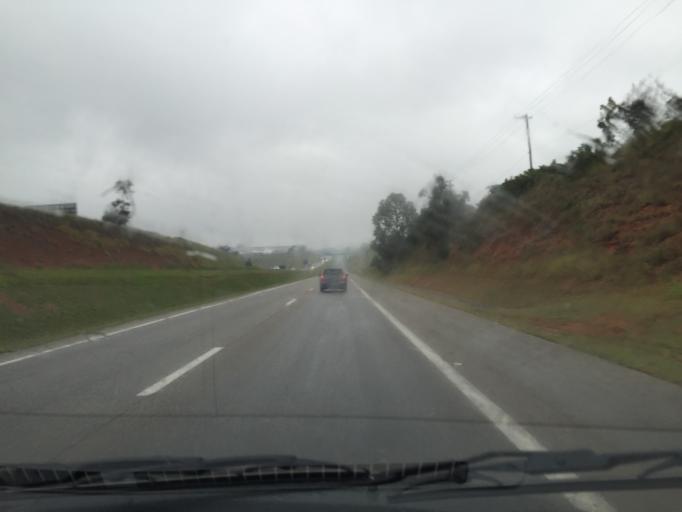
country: BR
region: Sao Paulo
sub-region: Itu
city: Itu
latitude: -23.3529
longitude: -47.3256
